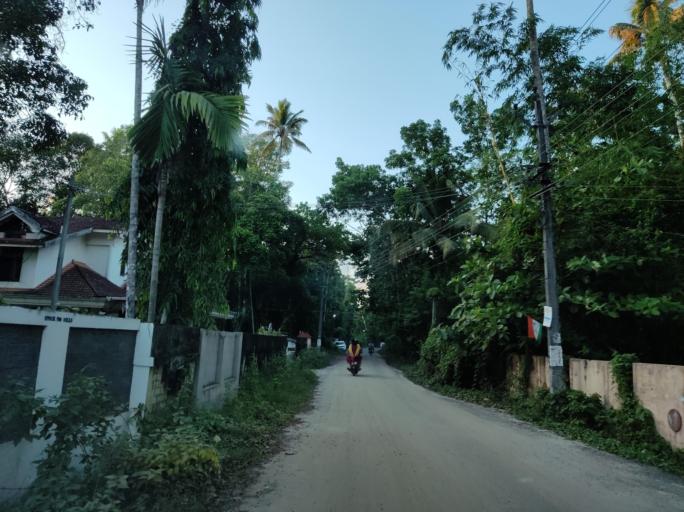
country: IN
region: Kerala
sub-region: Alappuzha
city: Vayalar
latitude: 9.7193
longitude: 76.2966
